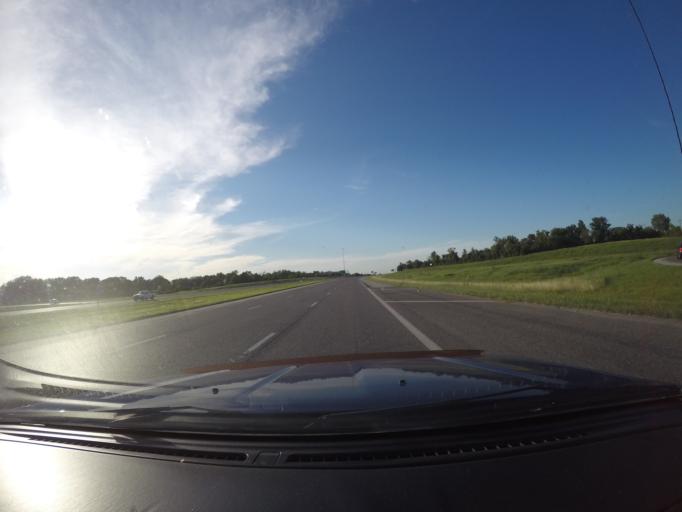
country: US
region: Kansas
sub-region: Wyandotte County
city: Edwardsville
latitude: 39.1297
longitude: -94.8168
